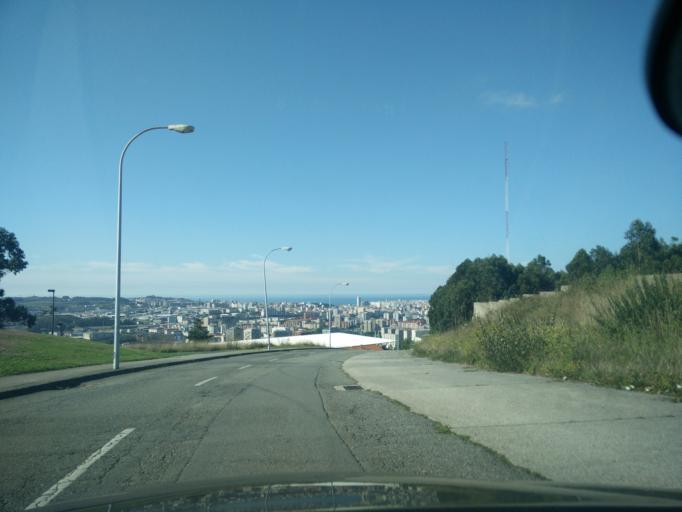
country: ES
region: Galicia
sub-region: Provincia da Coruna
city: Culleredo
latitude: 43.3264
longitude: -8.4068
